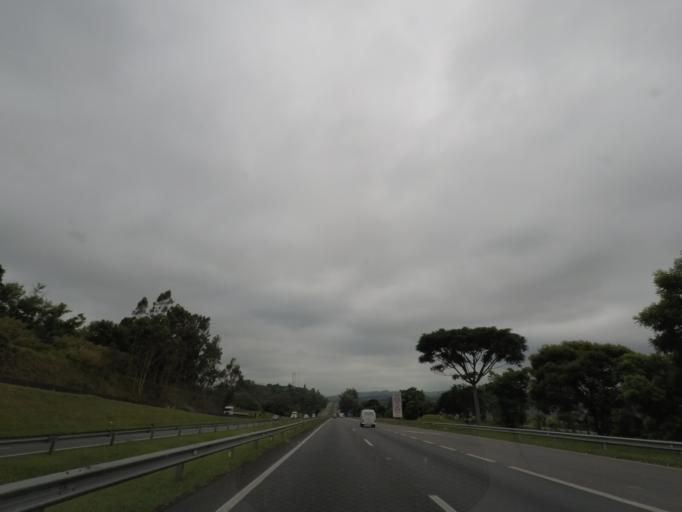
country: BR
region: Sao Paulo
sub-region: Itatiba
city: Itatiba
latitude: -22.9772
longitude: -46.8310
